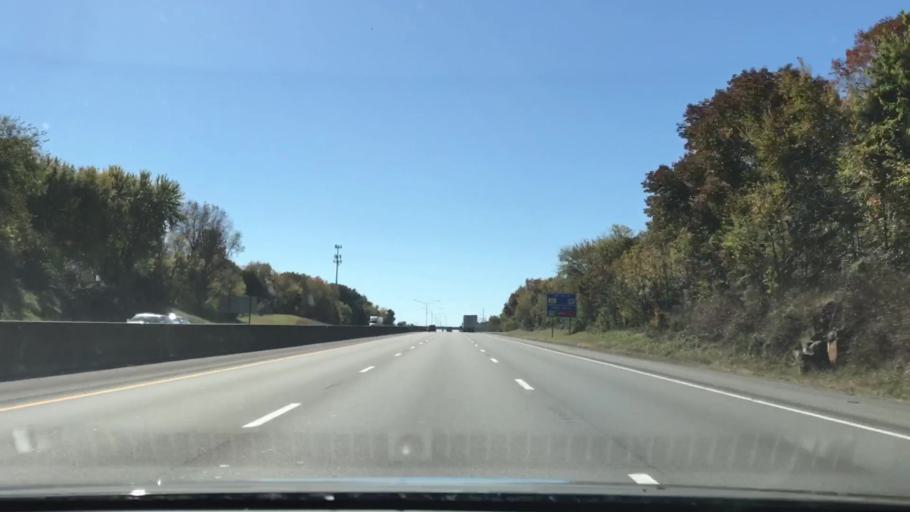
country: US
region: Kentucky
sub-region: Warren County
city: Bowling Green
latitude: 36.9849
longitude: -86.3872
